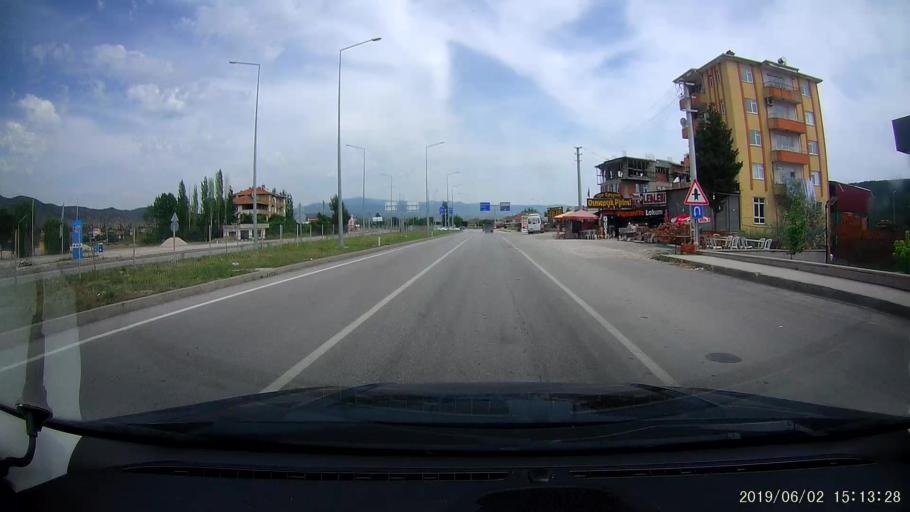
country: TR
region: Corum
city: Osmancik
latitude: 40.9721
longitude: 34.8217
